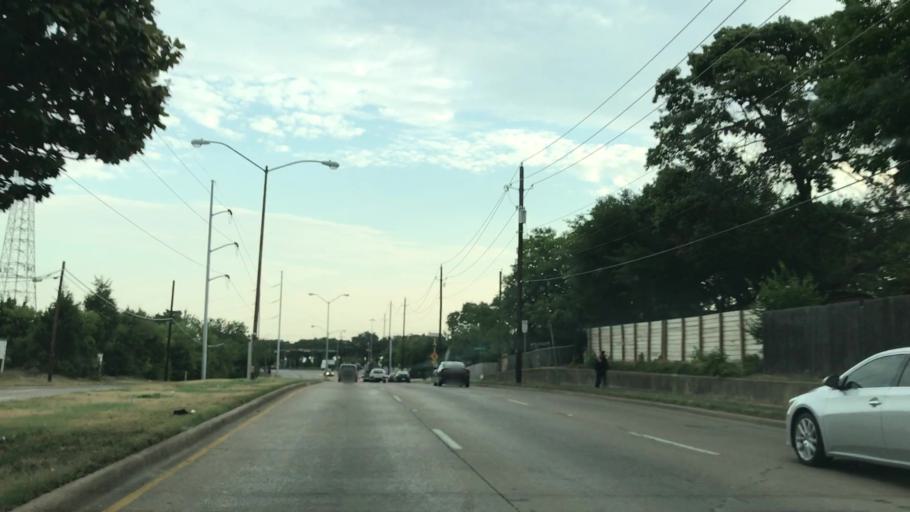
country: US
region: Texas
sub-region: Dallas County
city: Cockrell Hill
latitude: 32.7618
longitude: -96.8726
